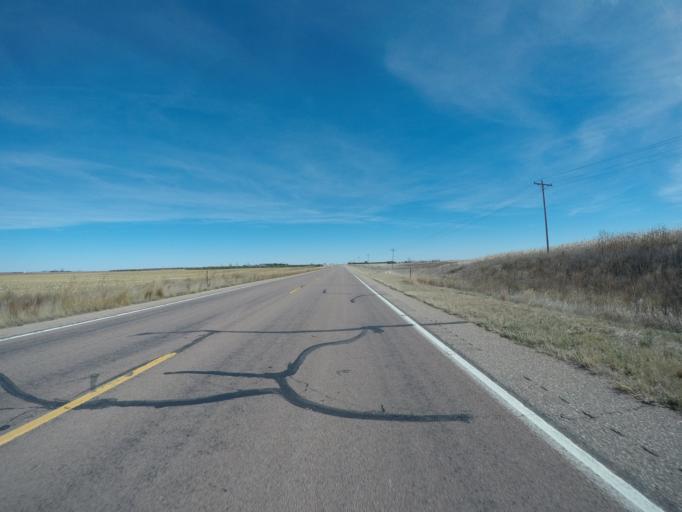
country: US
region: Colorado
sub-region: Yuma County
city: Yuma
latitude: 39.6559
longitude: -102.6447
